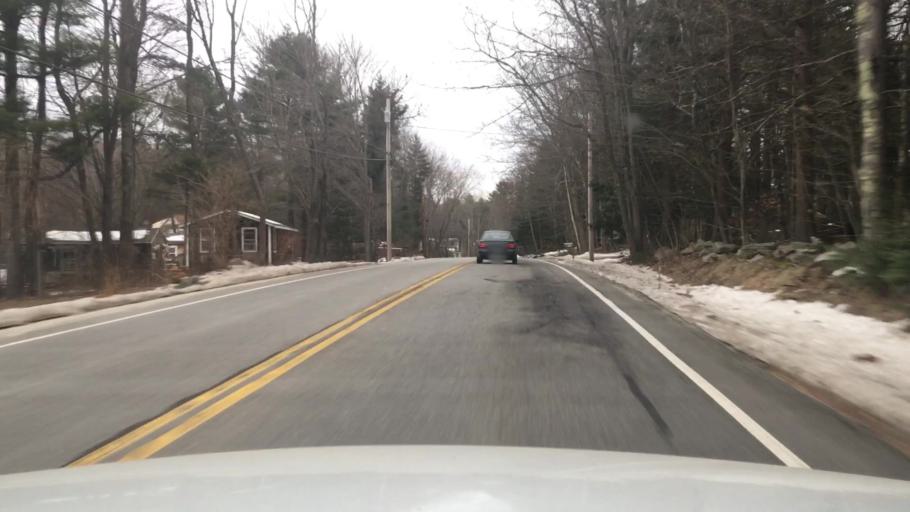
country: US
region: Maine
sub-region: Cumberland County
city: Freeport
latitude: 43.8753
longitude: -70.0574
